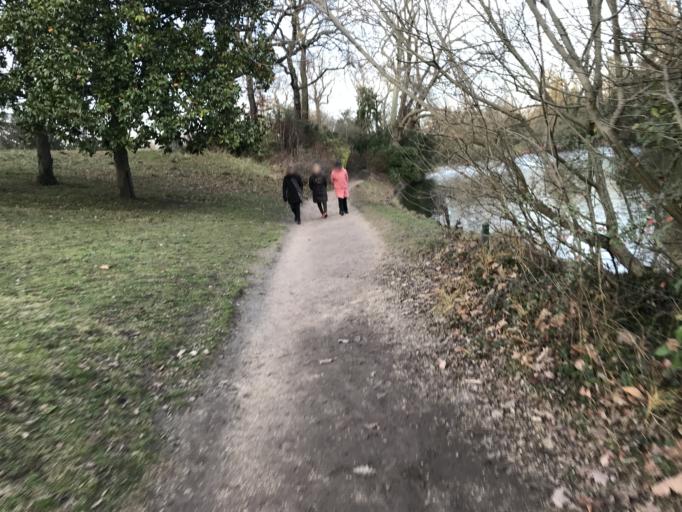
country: FR
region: Ile-de-France
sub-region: Departement des Hauts-de-Seine
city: Neuilly-sur-Seine
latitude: 48.8601
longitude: 2.2583
